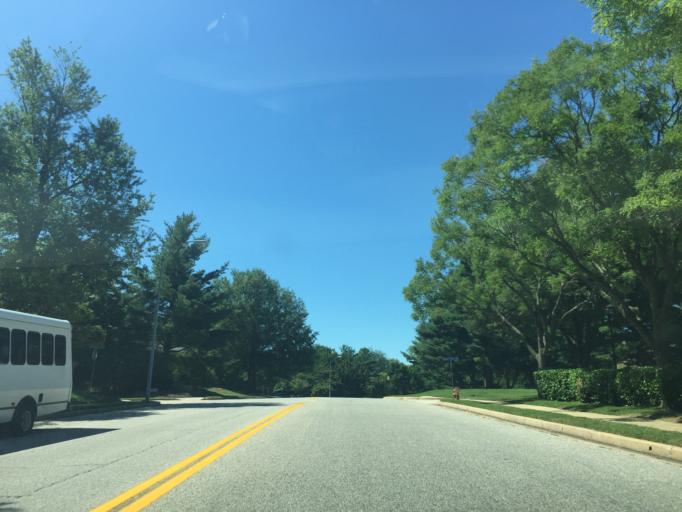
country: US
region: Maryland
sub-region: Baltimore County
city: Cockeysville
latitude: 39.4704
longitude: -76.6117
